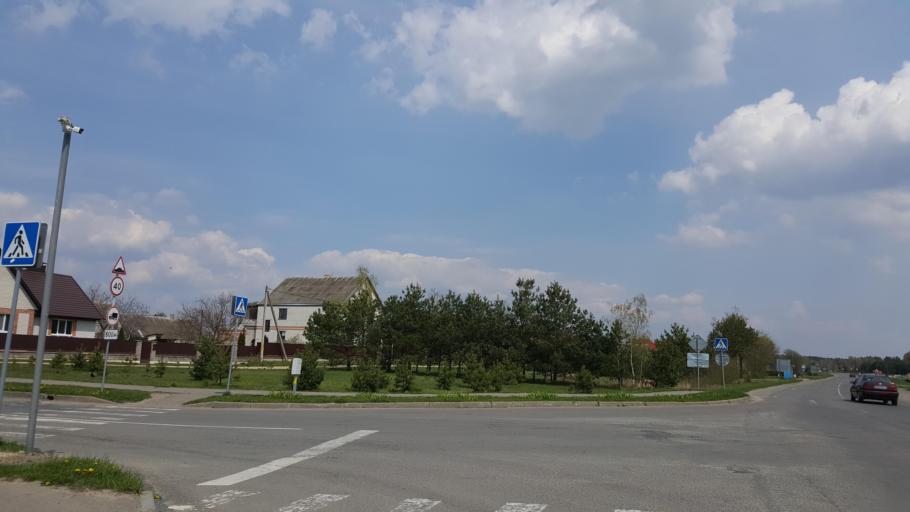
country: BY
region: Brest
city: Zhabinka
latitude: 52.1983
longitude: 24.0307
